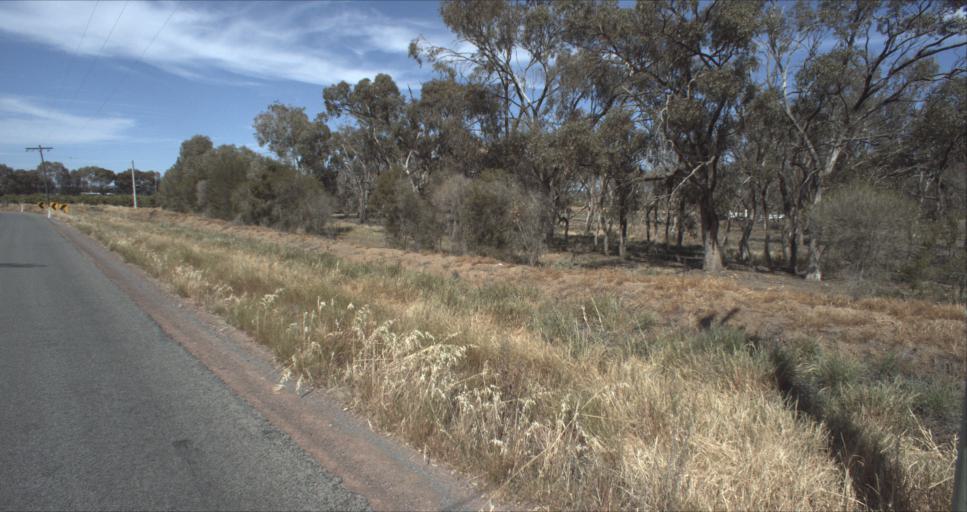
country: AU
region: New South Wales
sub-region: Leeton
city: Leeton
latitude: -34.5763
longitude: 146.4674
